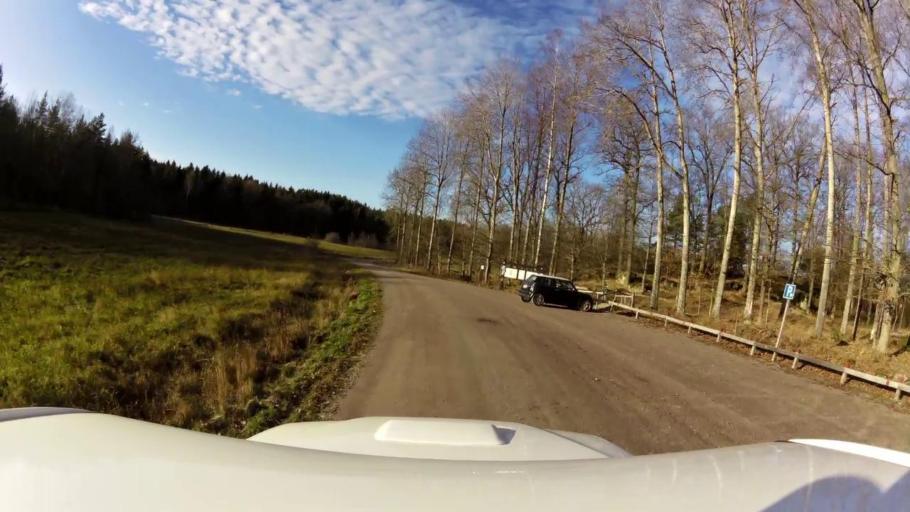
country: SE
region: OEstergoetland
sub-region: Linkopings Kommun
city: Linkoping
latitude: 58.3569
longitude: 15.6095
